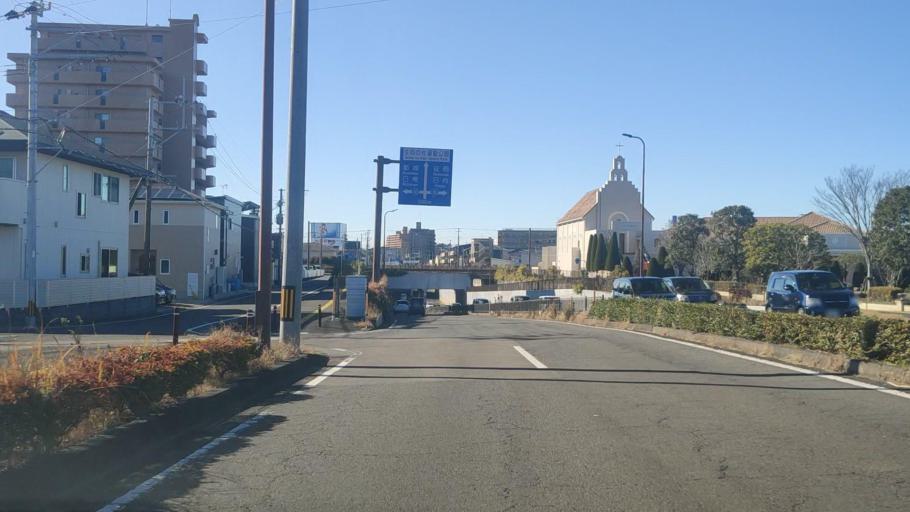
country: JP
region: Miyazaki
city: Miyazaki-shi
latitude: 31.9430
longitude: 131.4339
